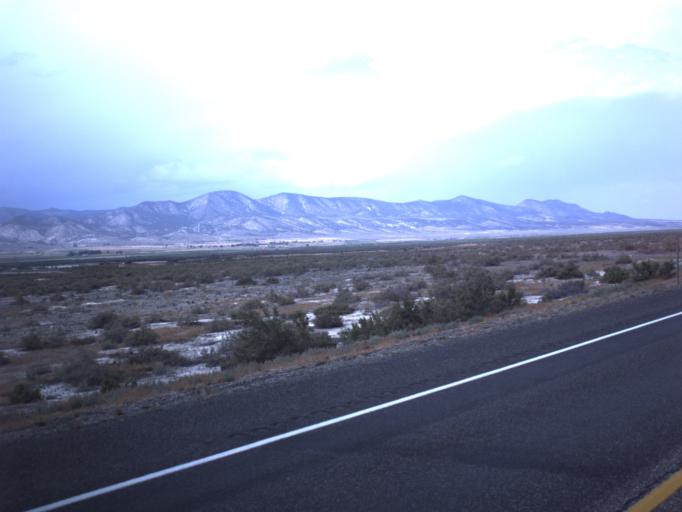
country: US
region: Utah
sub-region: Sanpete County
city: Gunnison
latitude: 39.1911
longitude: -111.8429
